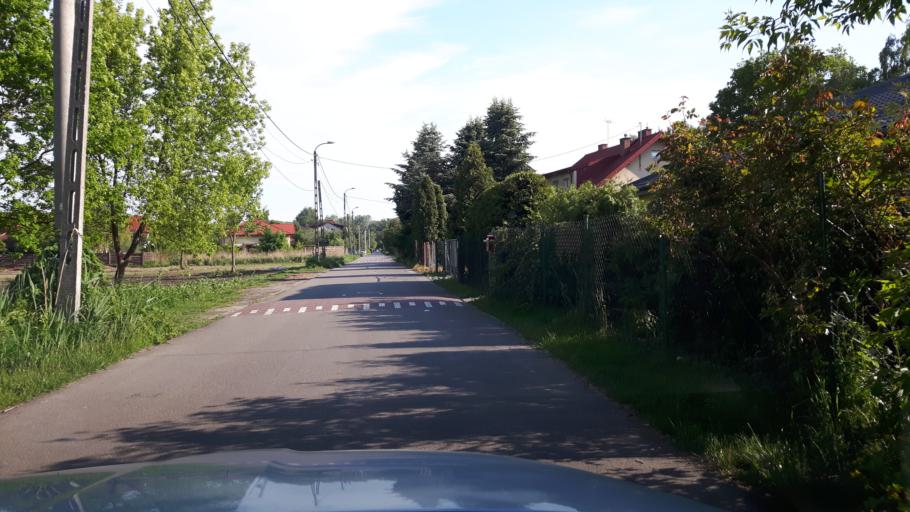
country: PL
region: Masovian Voivodeship
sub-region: Warszawa
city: Praga Poludnie
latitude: 52.2573
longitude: 21.1207
